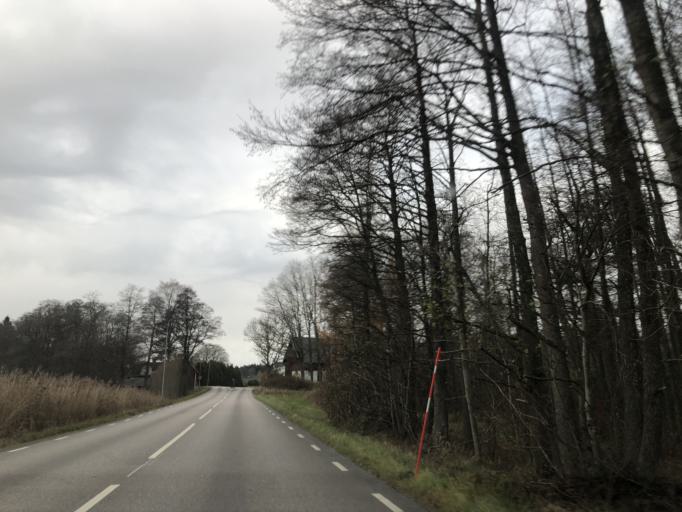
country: SE
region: Vaestra Goetaland
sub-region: Ulricehamns Kommun
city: Ulricehamn
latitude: 57.6783
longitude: 13.3897
